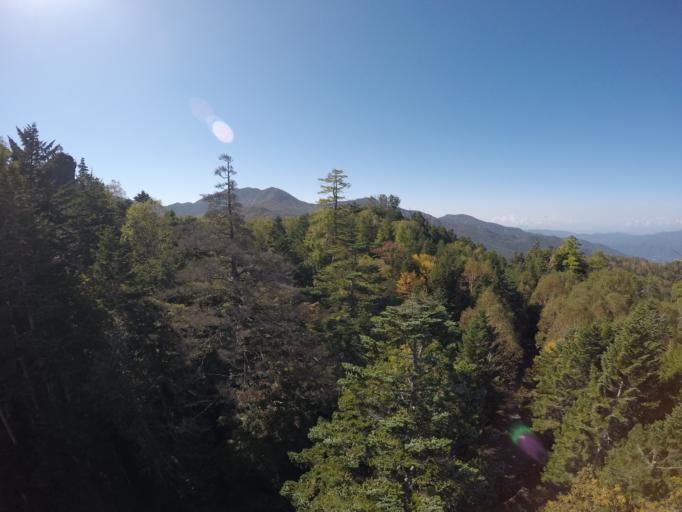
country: JP
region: Tochigi
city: Nikko
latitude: 36.8077
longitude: 139.3521
